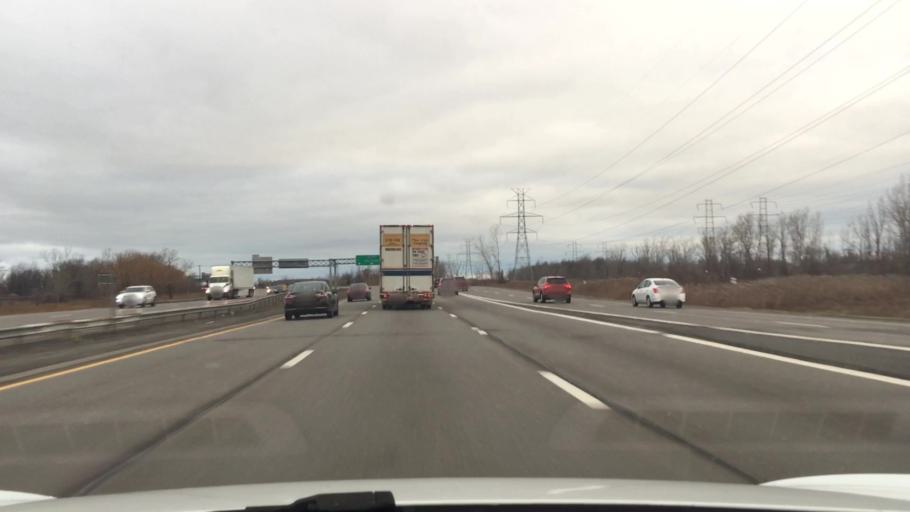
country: US
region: New York
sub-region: Erie County
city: Amherst
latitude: 43.0002
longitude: -78.8114
